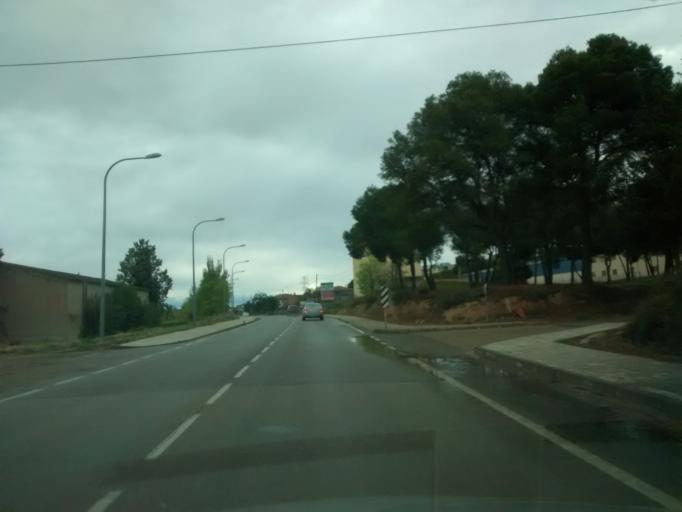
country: ES
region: Aragon
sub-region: Provincia de Zaragoza
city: Caspe
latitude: 41.2252
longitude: -0.0278
